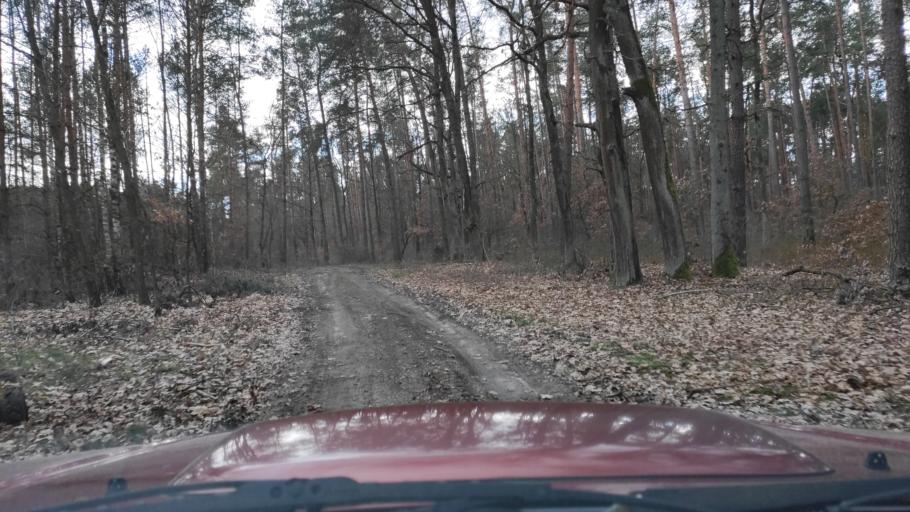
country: PL
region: Masovian Voivodeship
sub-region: Powiat kozienicki
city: Garbatka-Letnisko
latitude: 51.5139
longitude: 21.5645
